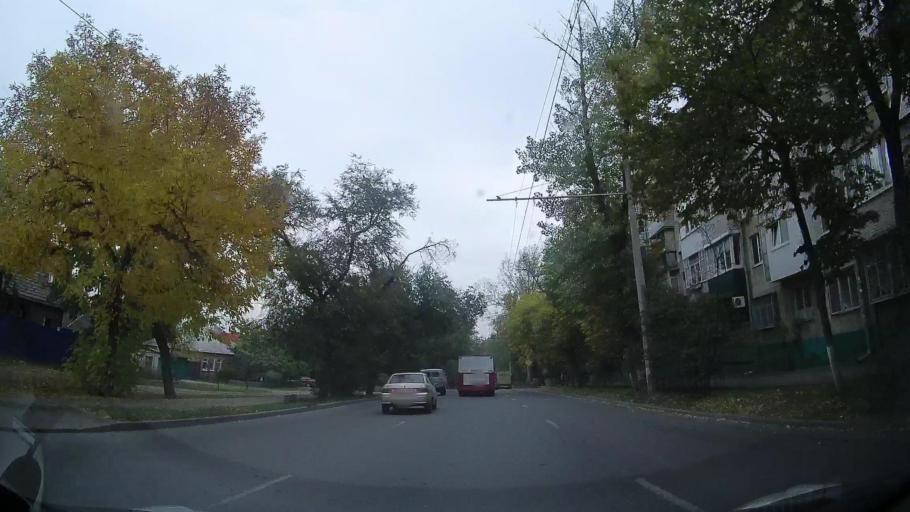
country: RU
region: Rostov
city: Severnyy
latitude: 47.2622
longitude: 39.6707
